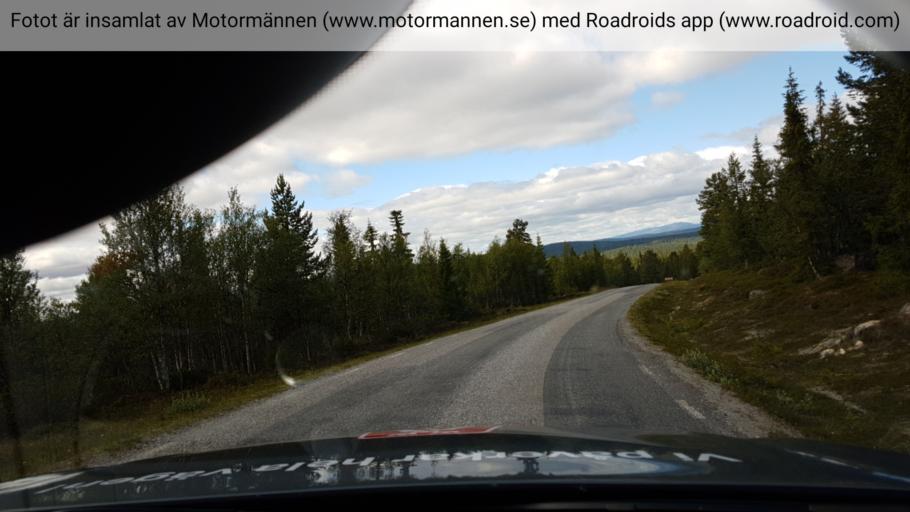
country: NO
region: Hedmark
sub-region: Engerdal
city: Engerdal
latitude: 62.2793
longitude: 12.8641
